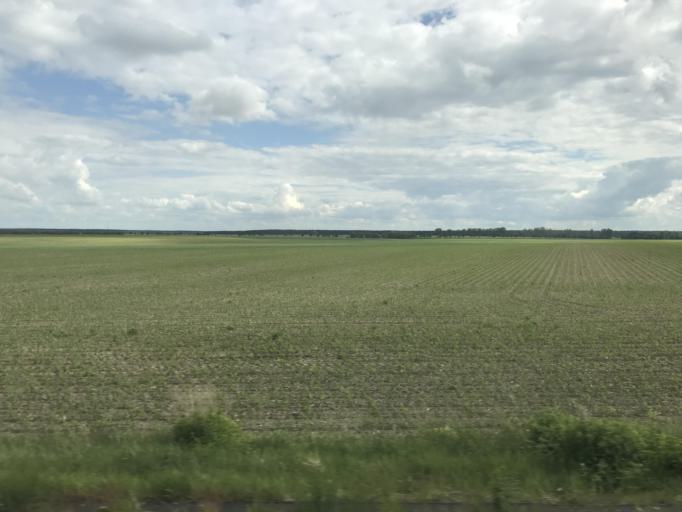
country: DE
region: Brandenburg
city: Niedergorsdorf
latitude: 51.9641
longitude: 12.9462
